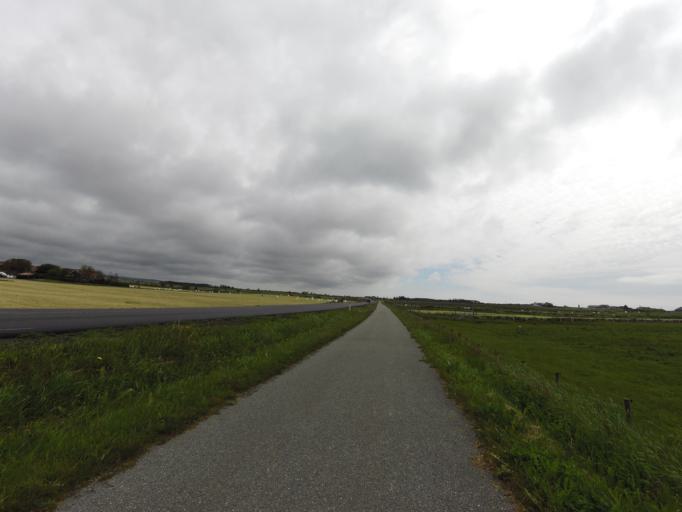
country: NO
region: Rogaland
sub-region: Ha
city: Naerbo
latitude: 58.6497
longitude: 5.6007
